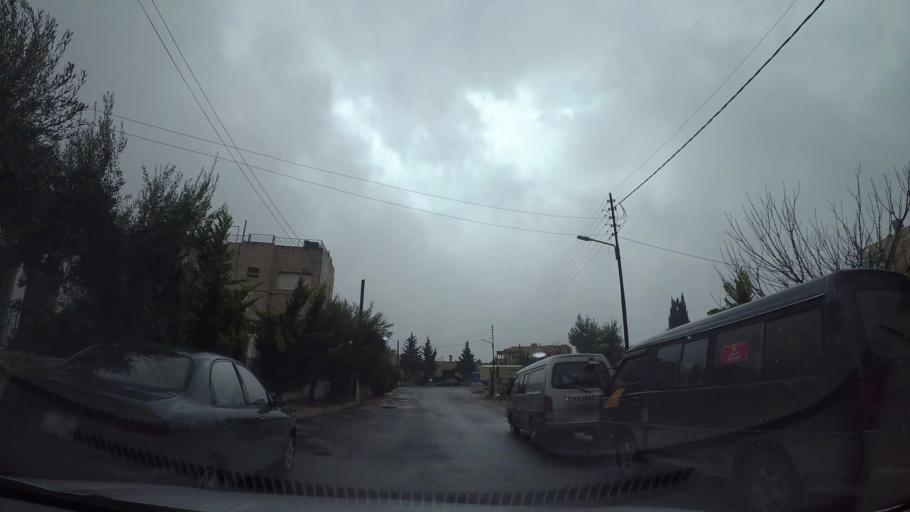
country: JO
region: Amman
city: Al Jubayhah
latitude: 32.0228
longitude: 35.8334
